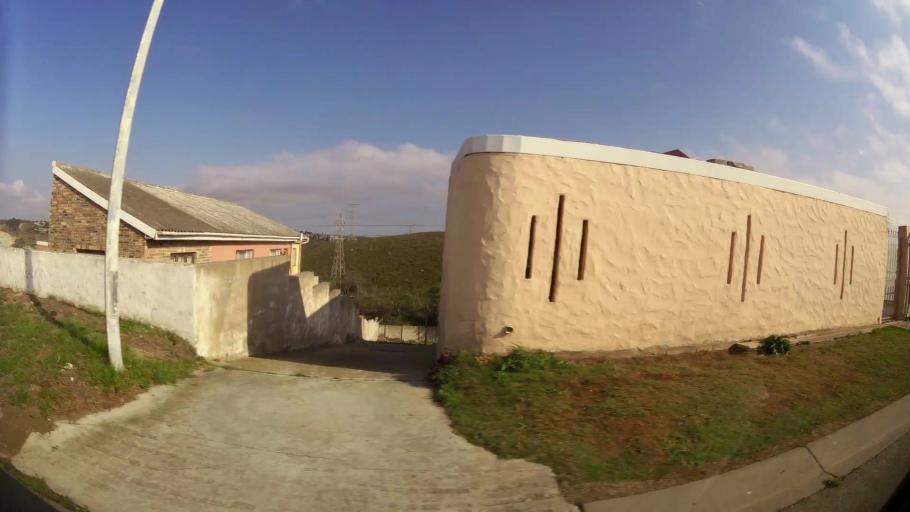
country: ZA
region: Eastern Cape
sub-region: Nelson Mandela Bay Metropolitan Municipality
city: Port Elizabeth
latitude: -33.9308
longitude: 25.5454
